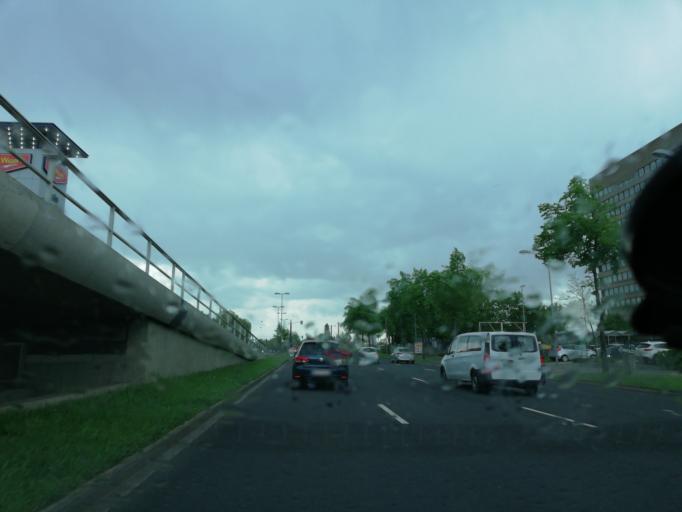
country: DE
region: North Rhine-Westphalia
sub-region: Regierungsbezirk Dusseldorf
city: Dusseldorf
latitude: 51.2089
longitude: 6.7578
